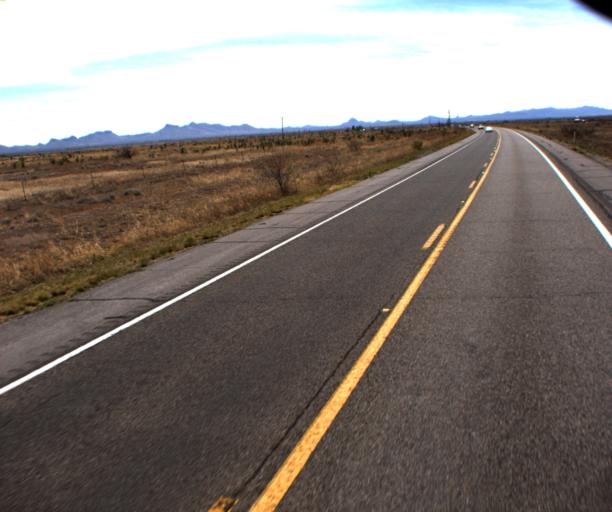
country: US
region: Arizona
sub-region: Cochise County
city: Pirtleville
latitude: 31.4550
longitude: -109.6099
